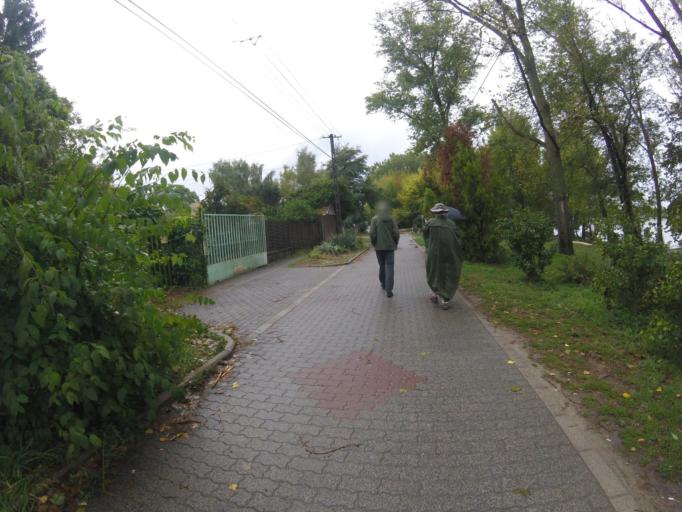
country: HU
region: Pest
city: Dunakeszi
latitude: 47.6529
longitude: 19.1202
